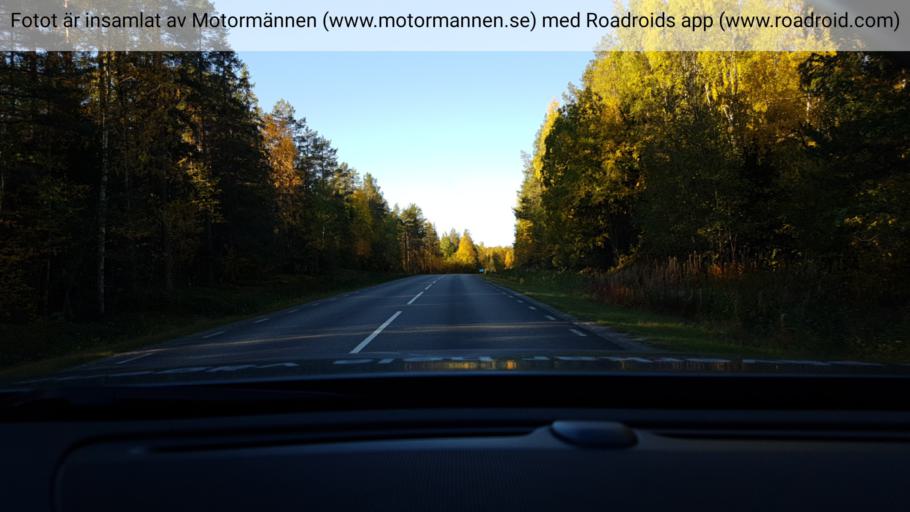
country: SE
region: Norrbotten
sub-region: Pitea Kommun
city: Roknas
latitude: 65.3557
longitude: 21.0470
